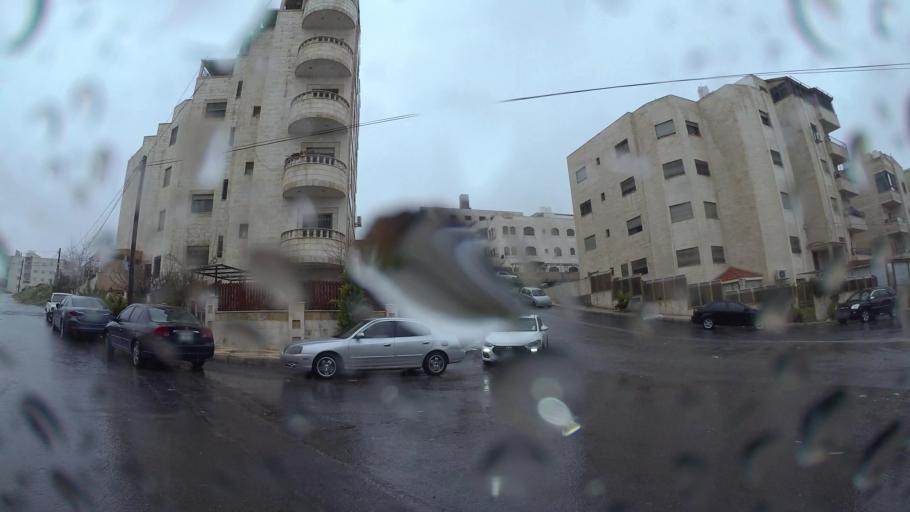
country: JO
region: Amman
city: Al Jubayhah
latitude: 32.0330
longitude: 35.8868
